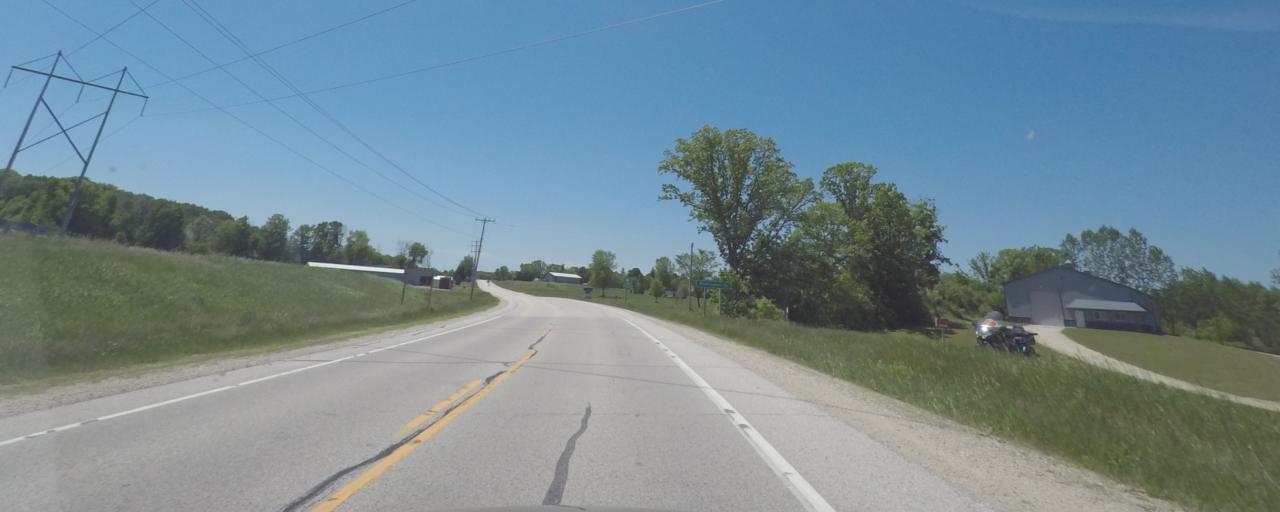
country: US
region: Wisconsin
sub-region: Ozaukee County
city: Kohler
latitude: 43.5426
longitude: -88.0855
